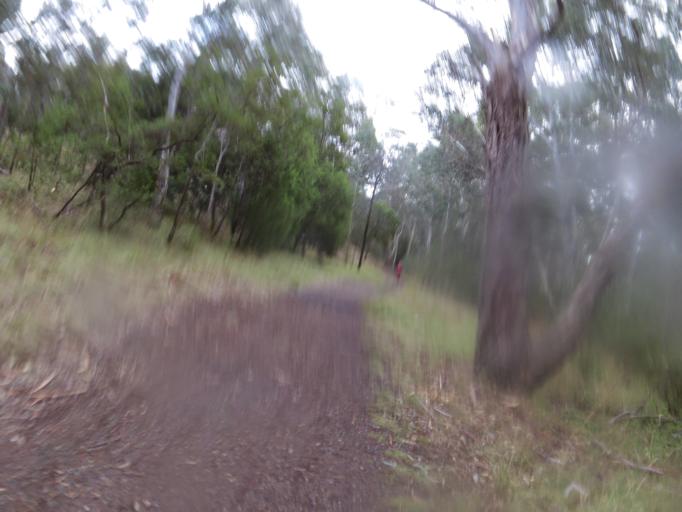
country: AU
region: Victoria
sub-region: Darebin
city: Fairfield
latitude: -37.7881
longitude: 145.0153
